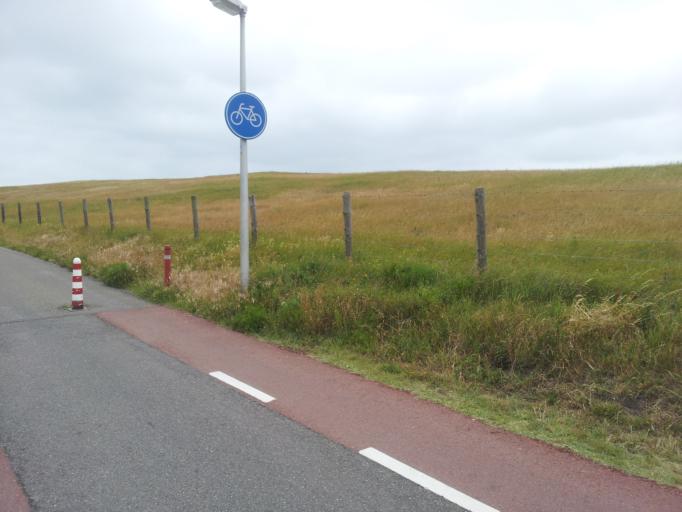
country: NL
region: South Holland
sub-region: Gemeente Katwijk
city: Katwijk aan Zee
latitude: 52.2086
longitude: 4.4064
